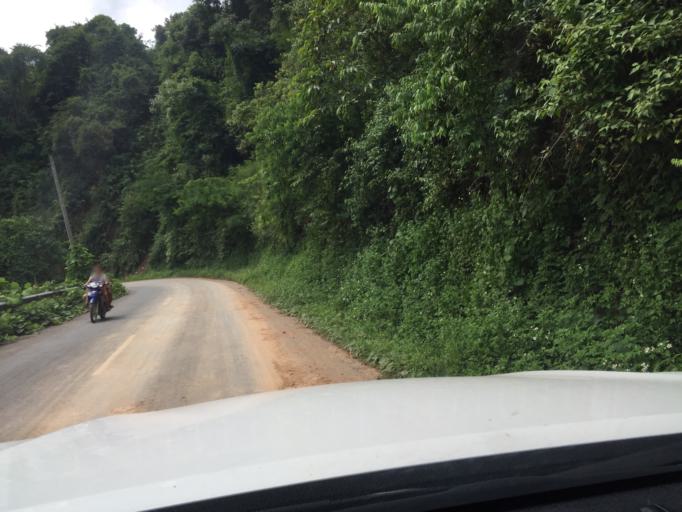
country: LA
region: Phongsali
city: Khoa
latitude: 21.1072
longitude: 102.2442
